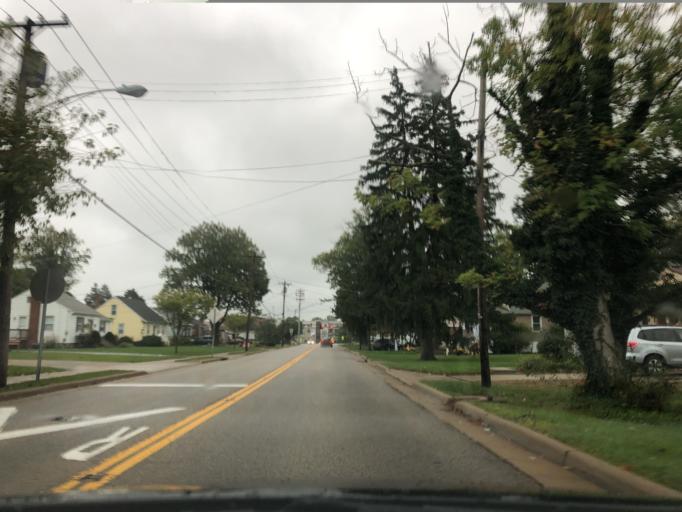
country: US
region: Ohio
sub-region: Hamilton County
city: Blue Ash
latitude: 39.2289
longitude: -84.3796
